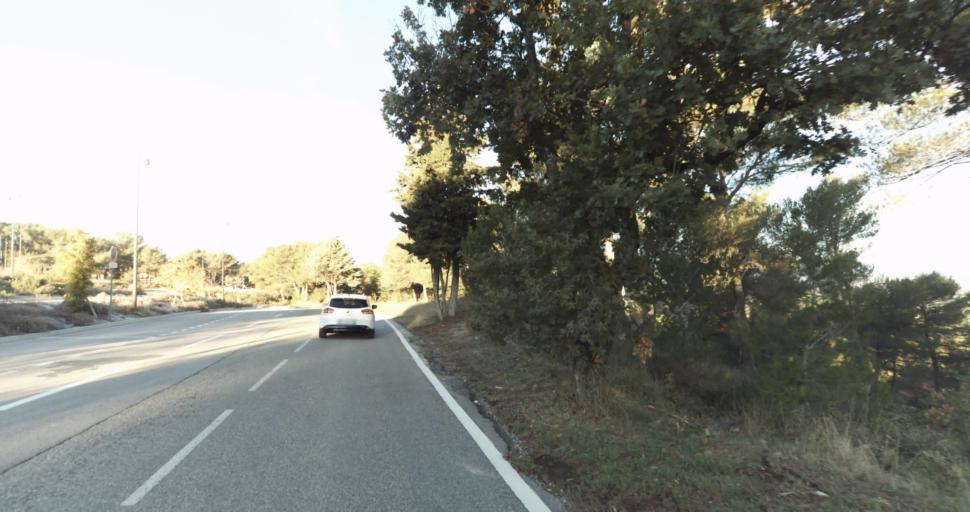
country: FR
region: Provence-Alpes-Cote d'Azur
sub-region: Departement des Bouches-du-Rhone
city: Venelles
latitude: 43.5979
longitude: 5.4960
